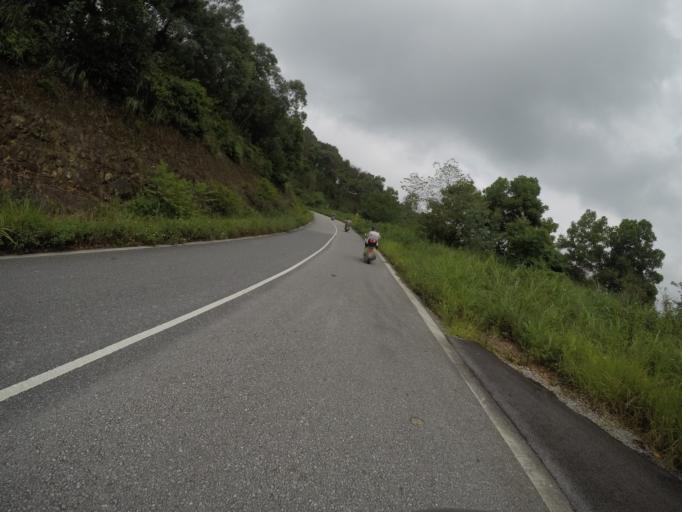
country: VN
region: Ha Noi
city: Soc Son
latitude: 21.2871
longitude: 105.8255
